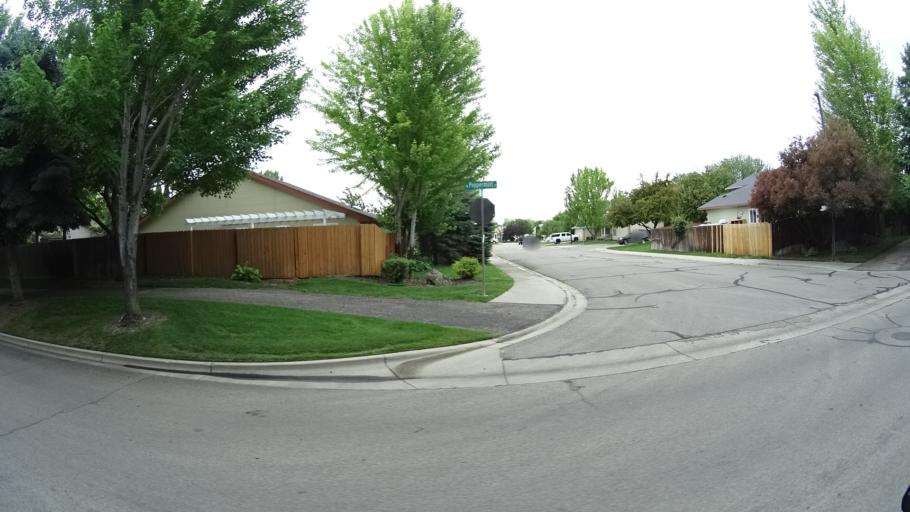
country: US
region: Idaho
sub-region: Ada County
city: Meridian
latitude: 43.5858
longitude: -116.3312
